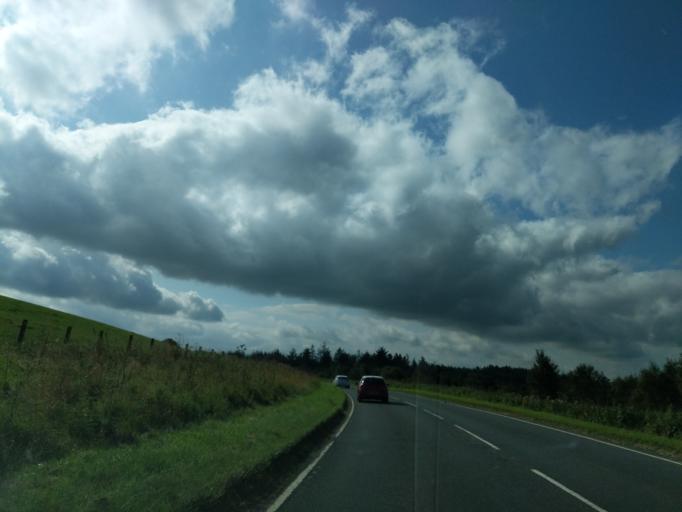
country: GB
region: Scotland
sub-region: Midlothian
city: Penicuik
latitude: 55.7795
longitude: -3.2190
